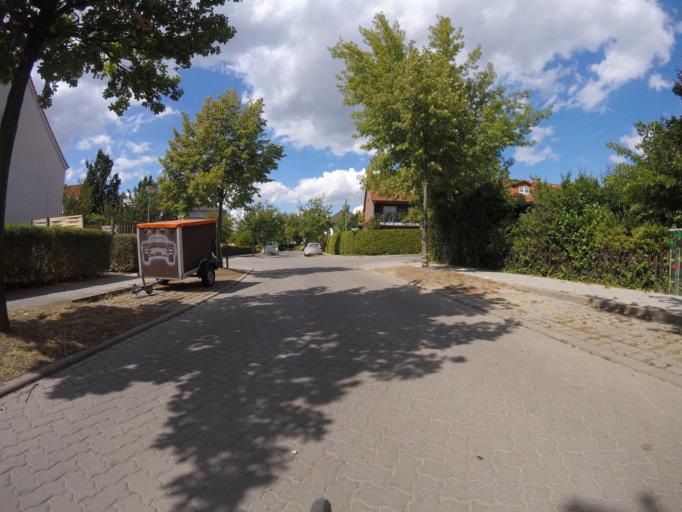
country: DE
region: Brandenburg
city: Werder
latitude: 52.4114
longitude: 12.9928
